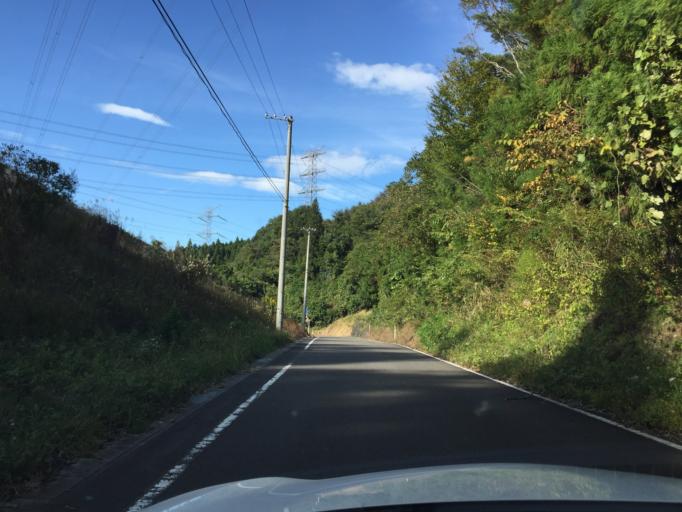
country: JP
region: Fukushima
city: Ishikawa
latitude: 37.1358
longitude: 140.5454
